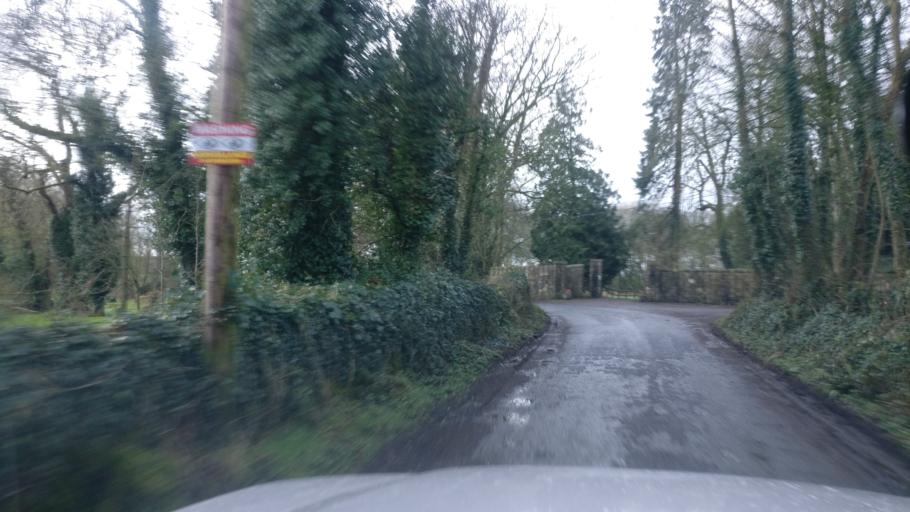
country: IE
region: Connaught
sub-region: County Galway
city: Athenry
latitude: 53.2719
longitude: -8.7722
